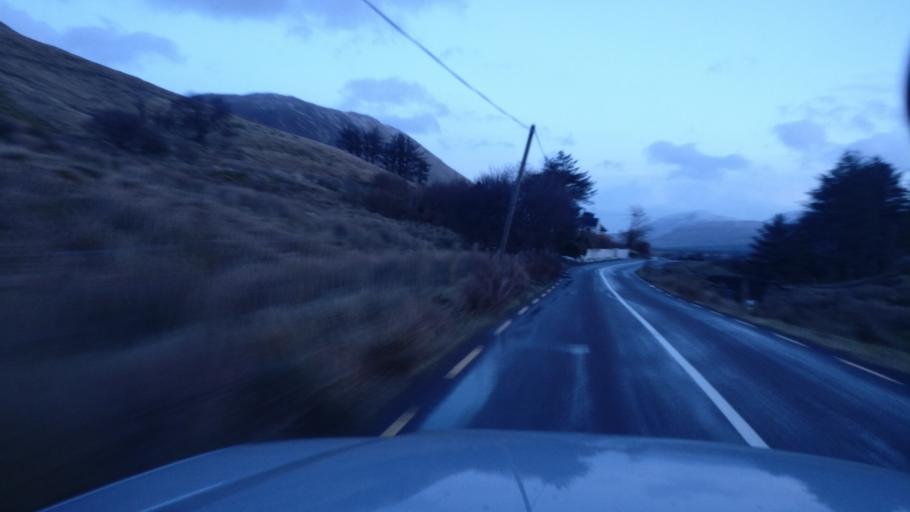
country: IE
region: Connaught
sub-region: Maigh Eo
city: Westport
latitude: 53.5774
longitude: -9.6660
